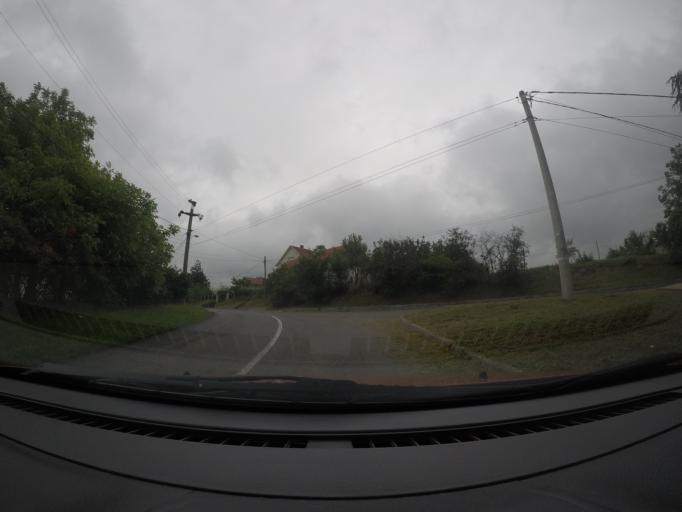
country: RS
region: Central Serbia
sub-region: Belgrade
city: Zvezdara
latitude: 44.6963
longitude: 20.5537
